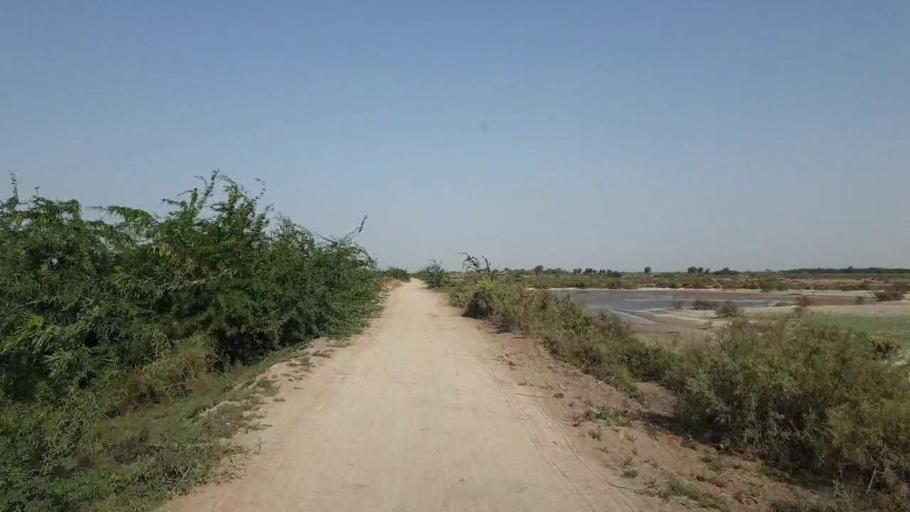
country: PK
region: Sindh
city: Tando Bago
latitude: 24.6433
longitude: 69.0721
